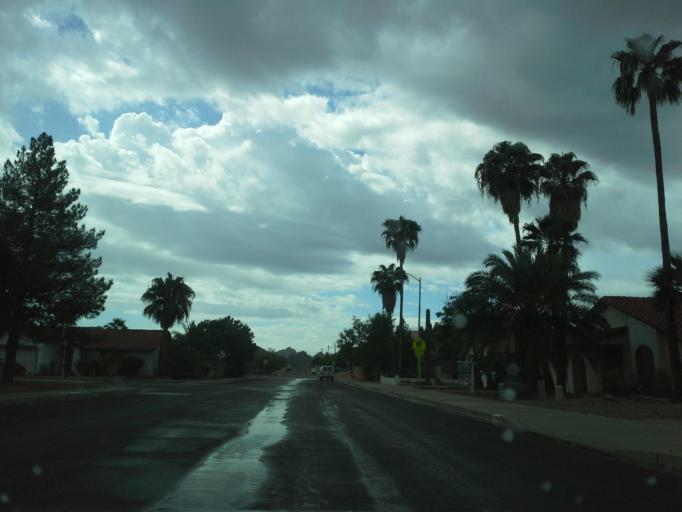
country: US
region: Arizona
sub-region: Maricopa County
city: Paradise Valley
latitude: 33.6125
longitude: -112.0394
